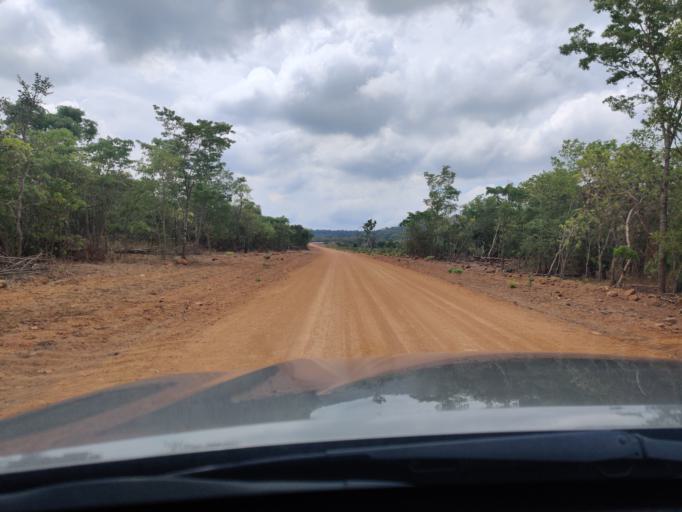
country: ZM
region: Central
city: Mkushi
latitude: -13.7783
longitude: 29.8504
